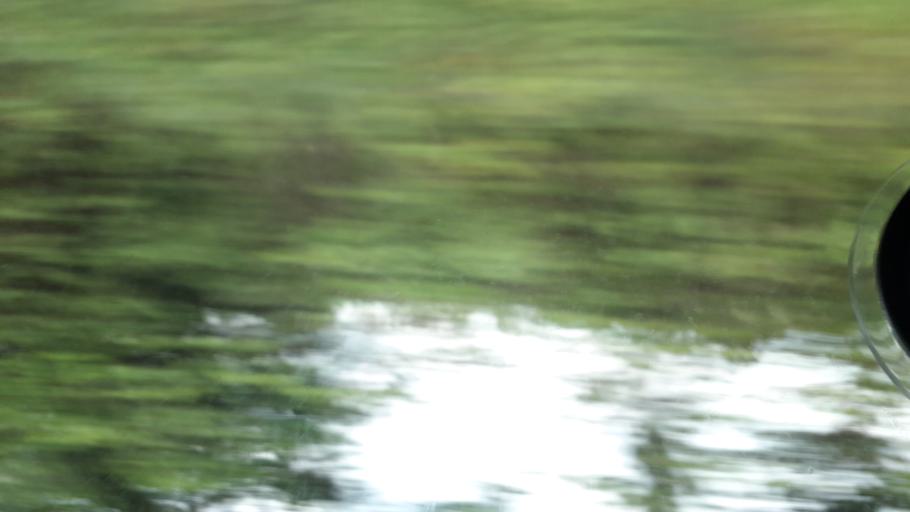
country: IE
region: Leinster
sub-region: Kildare
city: Celbridge
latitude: 53.3088
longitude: -6.5550
